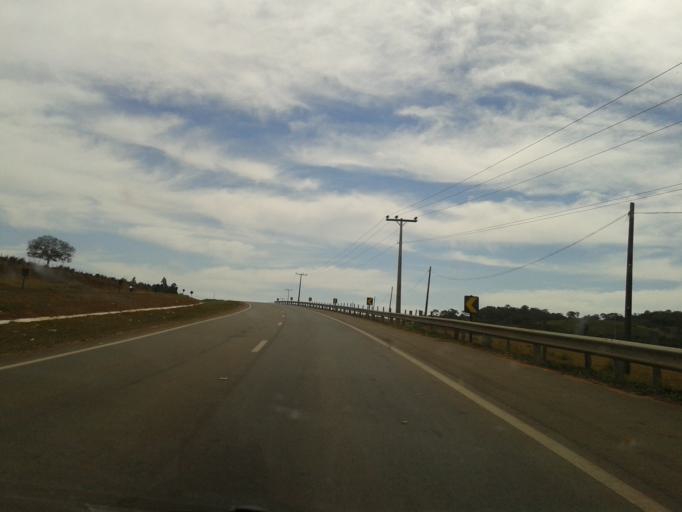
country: BR
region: Goias
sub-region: Inhumas
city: Inhumas
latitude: -16.1890
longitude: -49.6091
